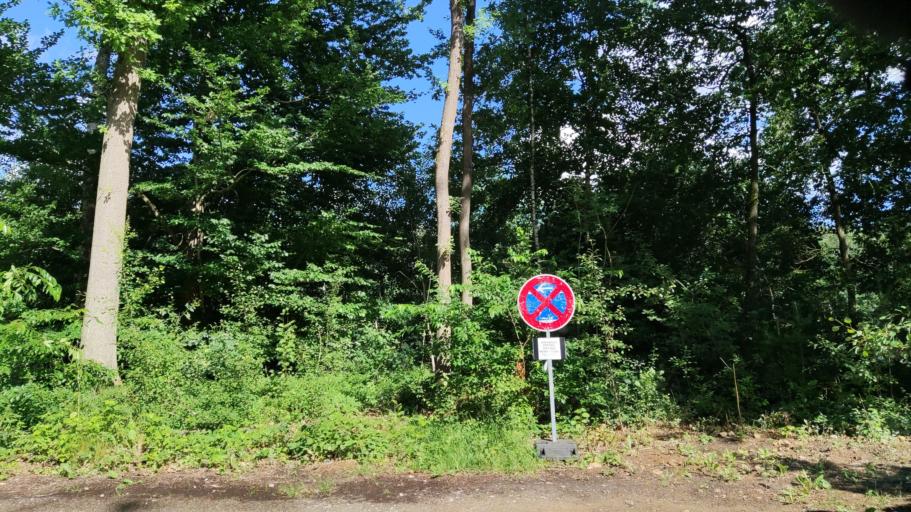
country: DE
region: Lower Saxony
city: Amelinghausen
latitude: 53.1302
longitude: 10.2304
